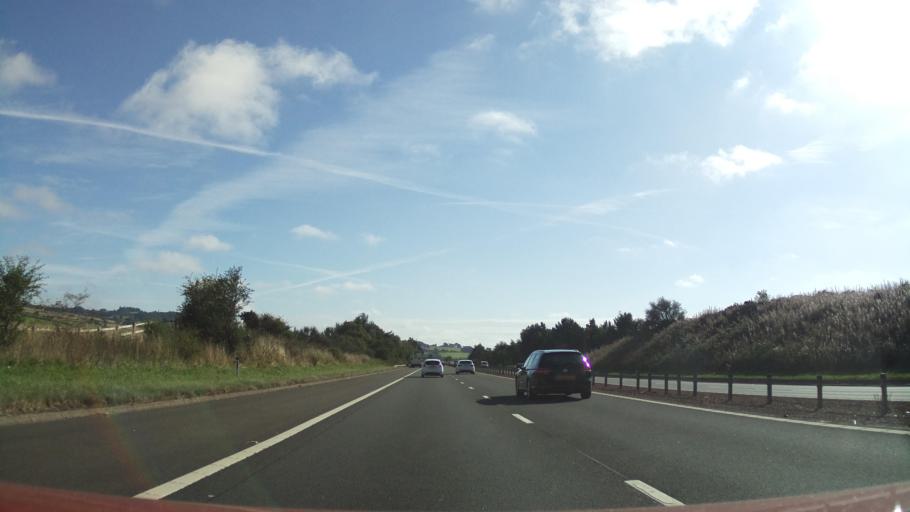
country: GB
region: Scotland
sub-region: Falkirk
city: Bo'ness
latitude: 55.9854
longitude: -3.6486
